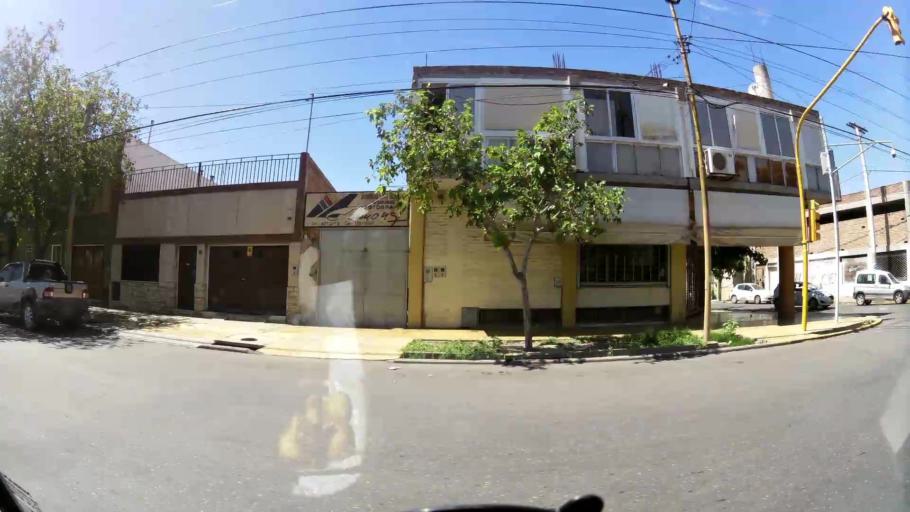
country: AR
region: San Juan
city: San Juan
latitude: -31.5302
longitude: -68.5221
